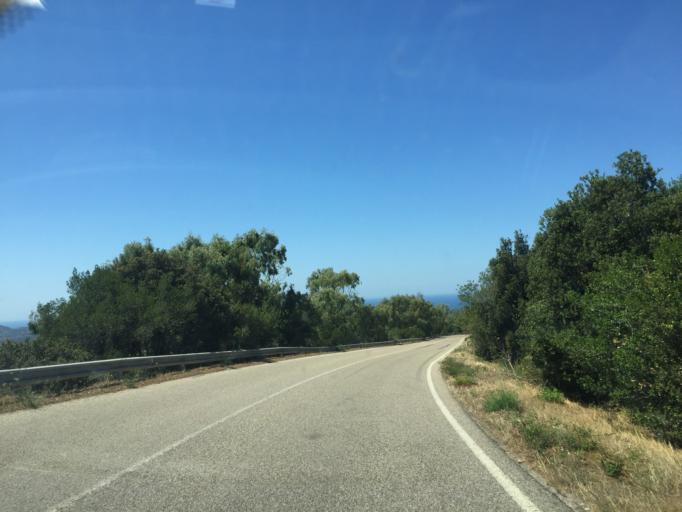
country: IT
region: Sardinia
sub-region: Provincia di Olbia-Tempio
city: Aglientu
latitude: 41.0890
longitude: 9.0993
